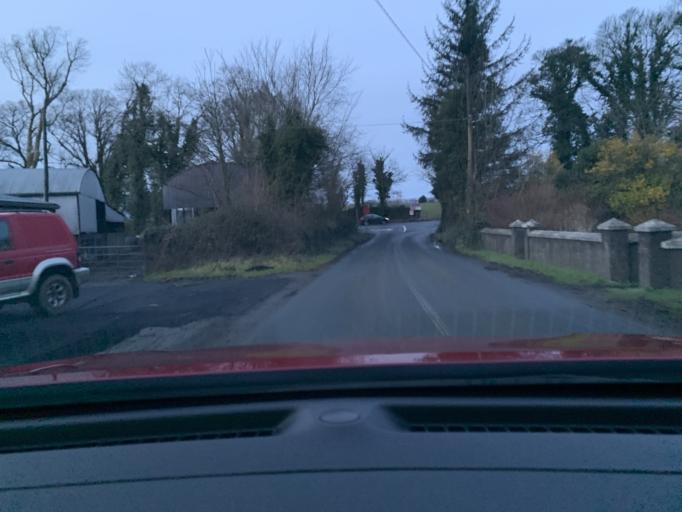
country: IE
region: Connaught
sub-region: Sligo
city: Sligo
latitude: 54.2647
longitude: -8.5084
